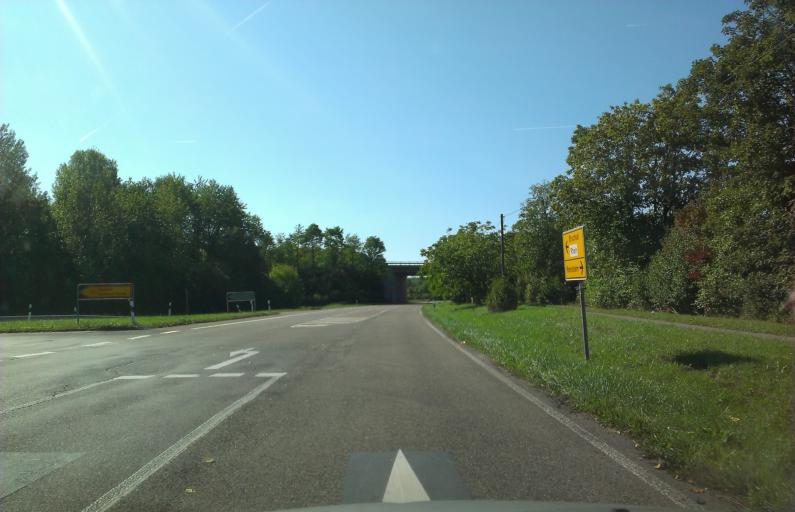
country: DE
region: Rheinland-Pfalz
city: Germersheim
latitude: 49.2279
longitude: 8.3992
